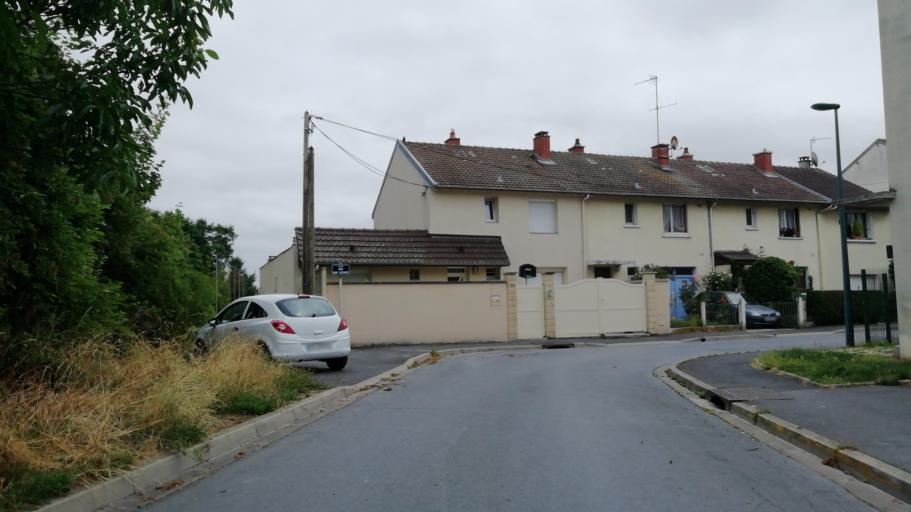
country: FR
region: Champagne-Ardenne
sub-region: Departement de la Marne
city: Betheny
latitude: 49.2567
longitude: 4.0644
